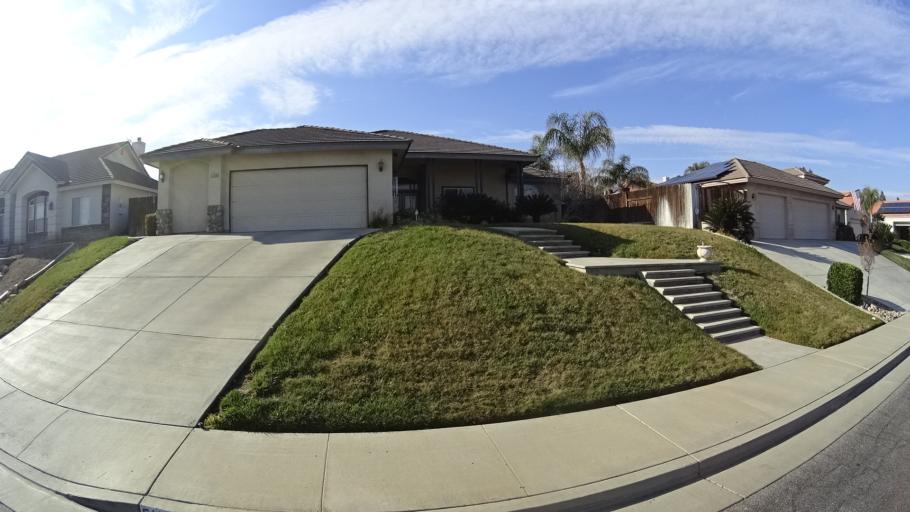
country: US
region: California
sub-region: Kern County
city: Oildale
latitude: 35.4004
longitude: -118.9171
